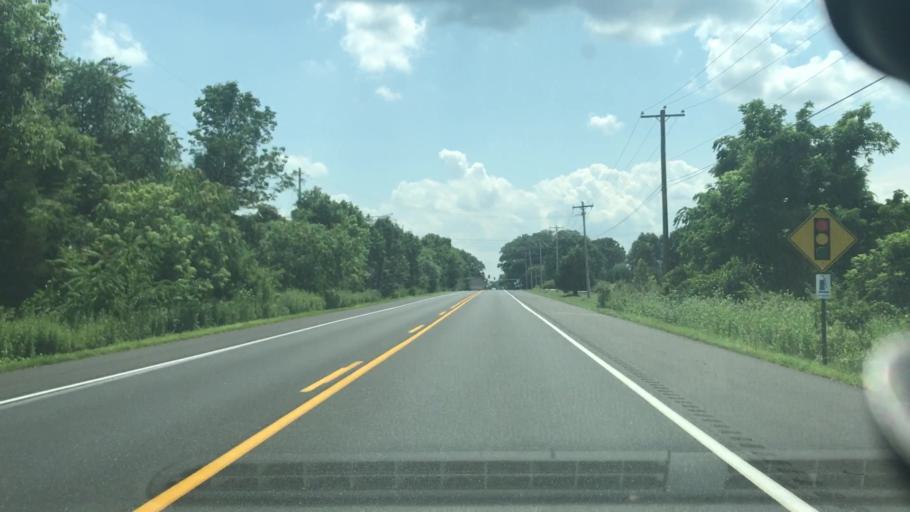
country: US
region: Pennsylvania
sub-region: Bucks County
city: New Hope
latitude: 40.3669
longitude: -74.9665
